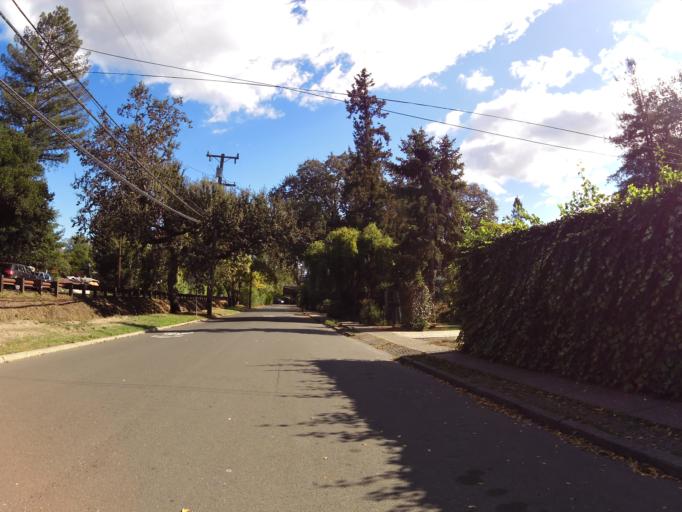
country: US
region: California
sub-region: Marin County
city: San Anselmo
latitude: 37.9789
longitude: -122.5713
